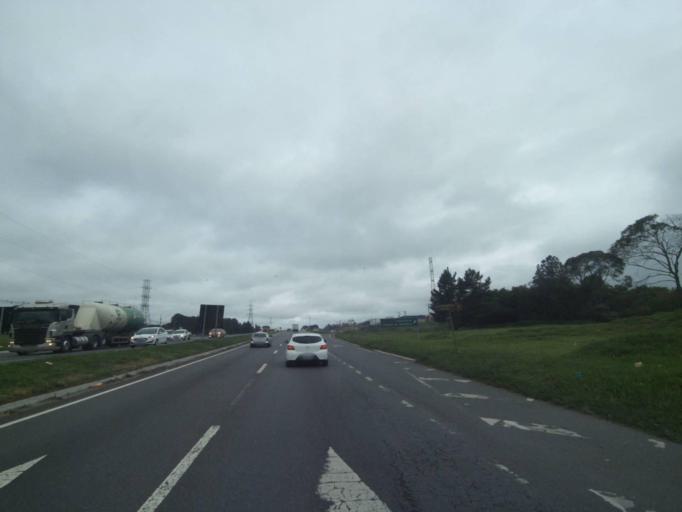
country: BR
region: Parana
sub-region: Araucaria
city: Araucaria
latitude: -25.5533
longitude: -49.3356
